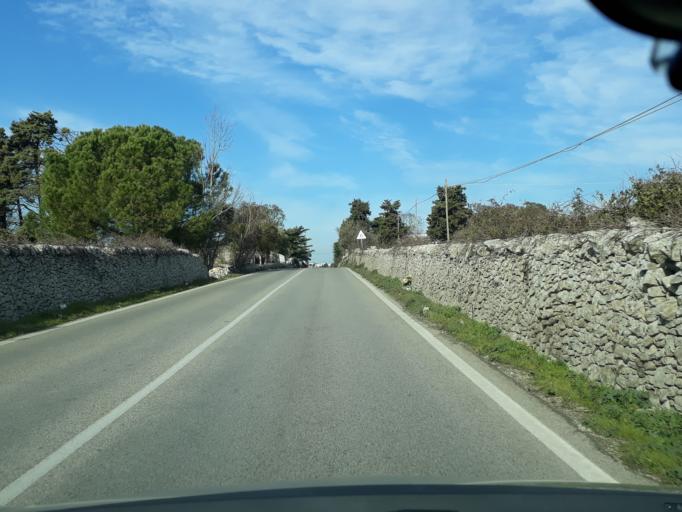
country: IT
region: Apulia
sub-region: Provincia di Taranto
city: Martina Franca
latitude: 40.7285
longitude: 17.3326
